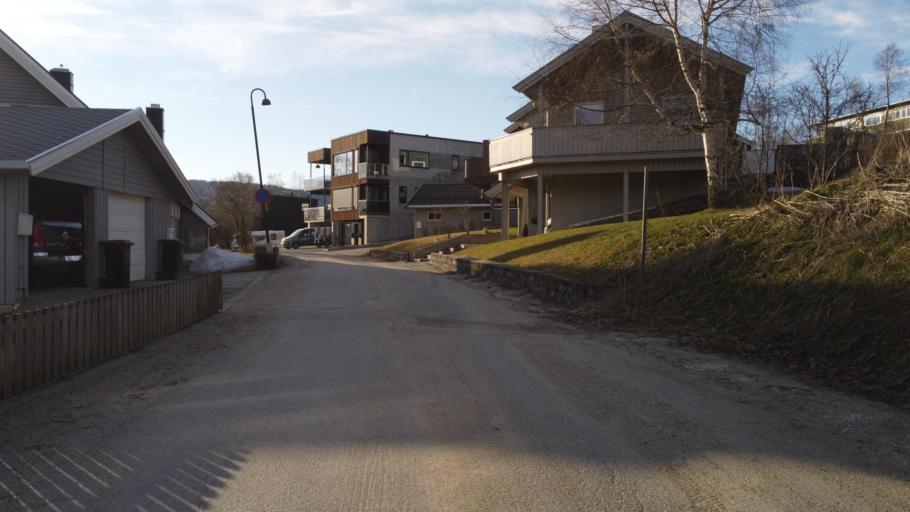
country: NO
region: Nordland
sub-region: Rana
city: Mo i Rana
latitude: 66.3135
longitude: 14.1394
